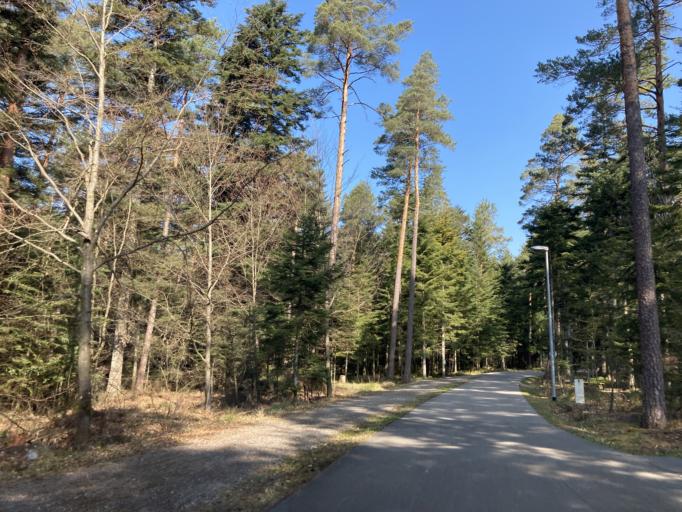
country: DE
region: Baden-Wuerttemberg
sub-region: Karlsruhe Region
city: Schomberg
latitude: 48.7805
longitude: 8.6327
